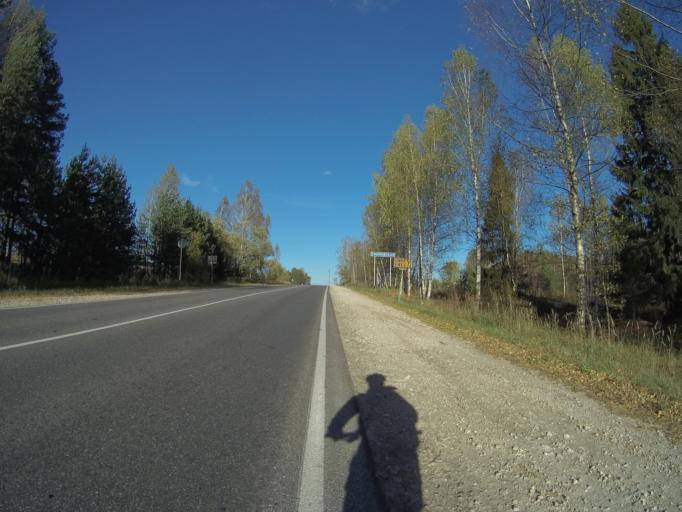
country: RU
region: Vladimir
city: Golovino
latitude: 55.9838
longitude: 40.5534
